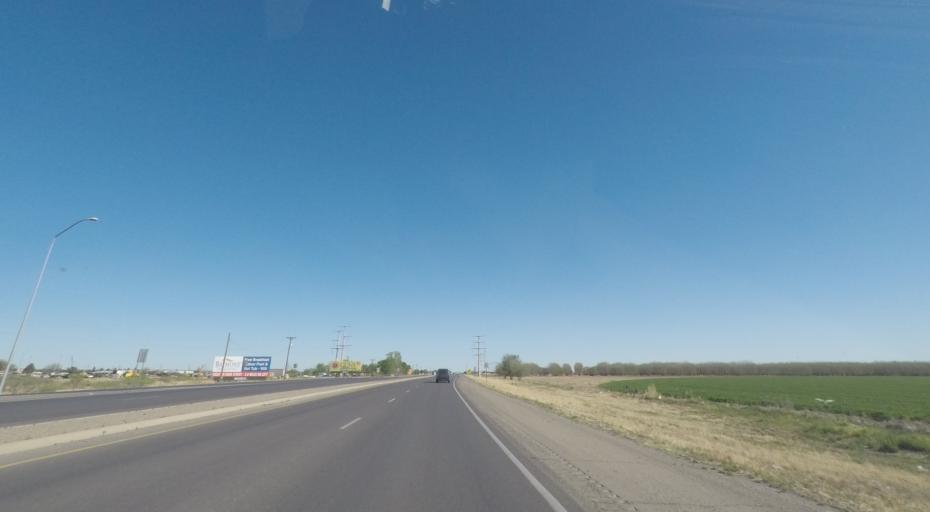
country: US
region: New Mexico
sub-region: Chaves County
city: Roswell
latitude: 33.3315
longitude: -104.5047
